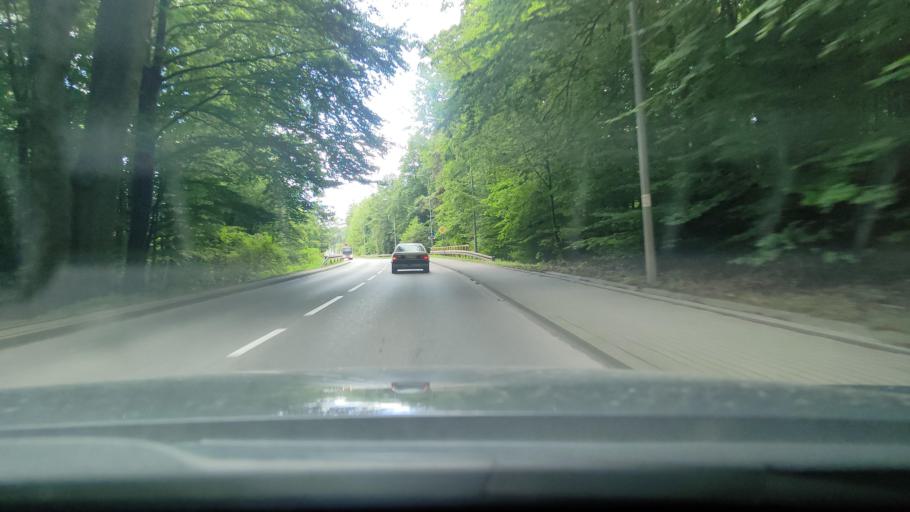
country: PL
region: Pomeranian Voivodeship
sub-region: Powiat wejherowski
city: Wejherowo
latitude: 54.5929
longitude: 18.2370
